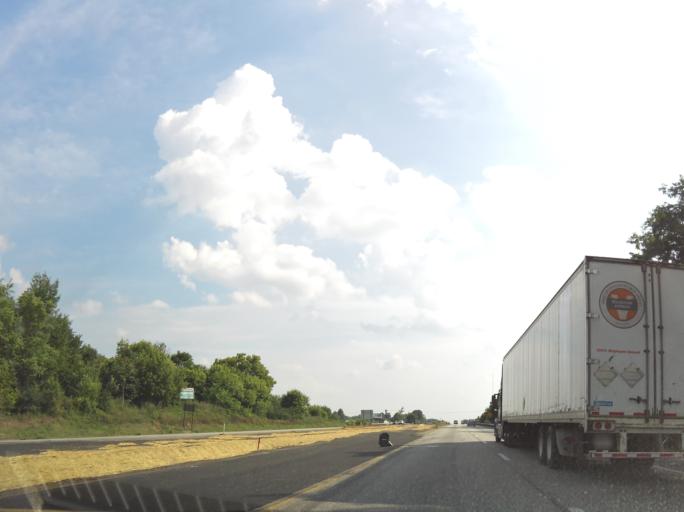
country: US
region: Pennsylvania
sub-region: Franklin County
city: Greencastle
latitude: 39.7801
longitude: -77.7159
